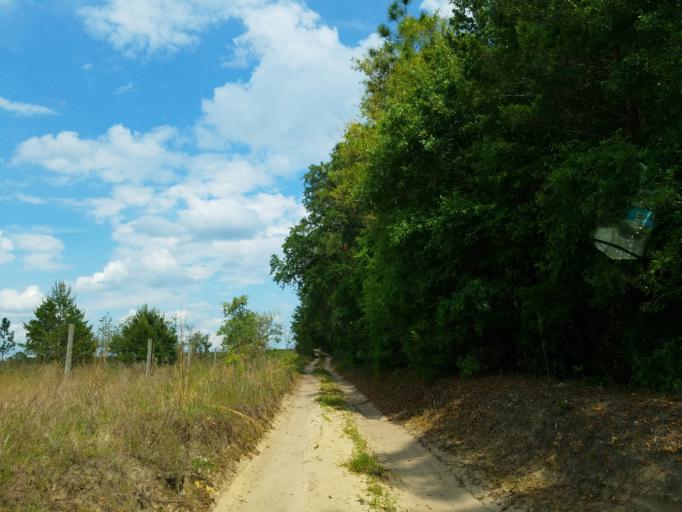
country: US
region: Florida
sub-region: Hernando County
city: Hill 'n Dale
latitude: 28.5502
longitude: -82.2665
